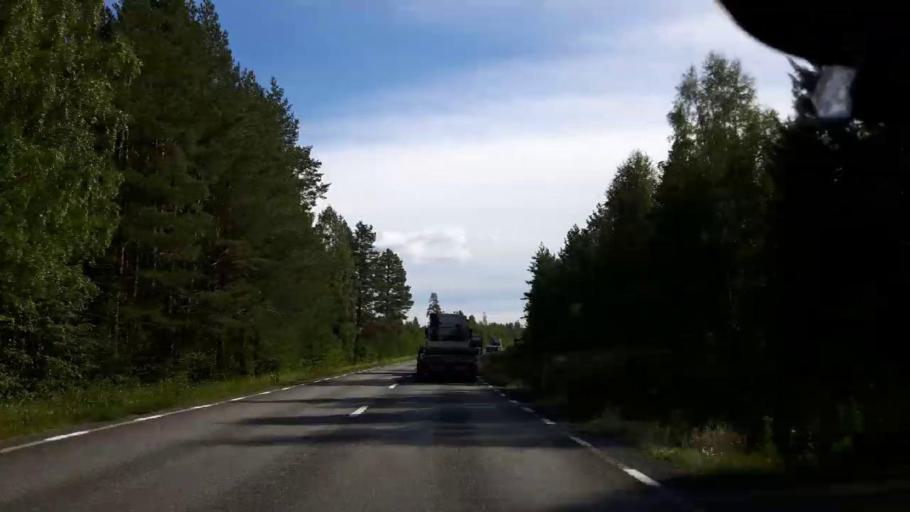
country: SE
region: Jaemtland
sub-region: Braecke Kommun
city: Braecke
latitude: 63.1926
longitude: 15.4319
